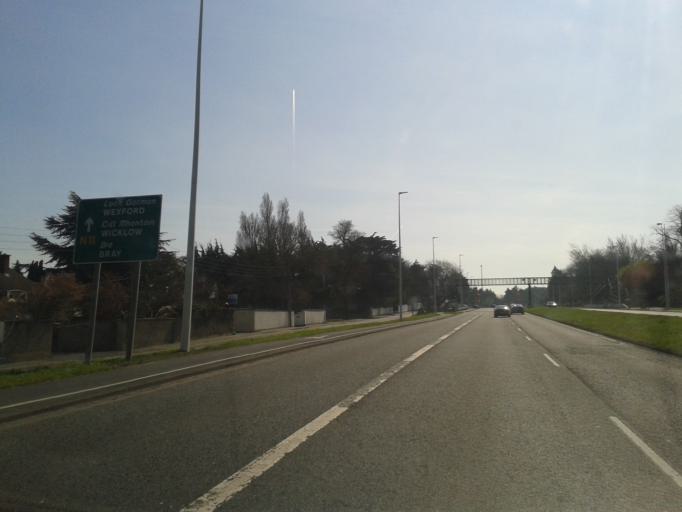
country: IE
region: Leinster
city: Mount Merrion
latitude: 53.3065
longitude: -6.2127
